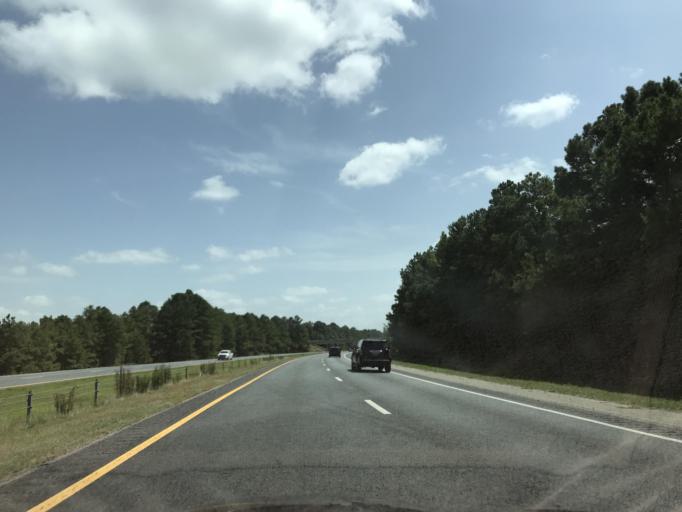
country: US
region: North Carolina
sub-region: Johnston County
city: Four Oaks
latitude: 35.3235
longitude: -78.4228
